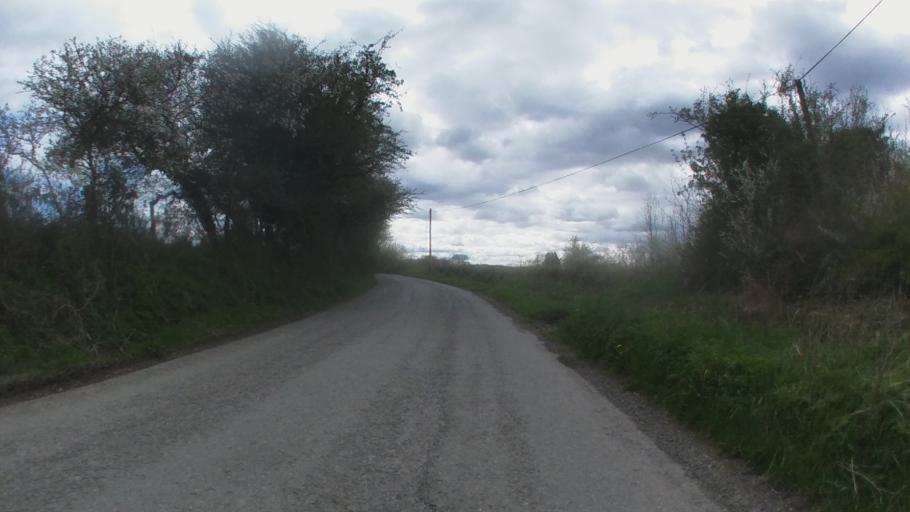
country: IE
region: Leinster
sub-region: Kilkenny
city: Kilkenny
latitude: 52.7251
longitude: -7.2309
